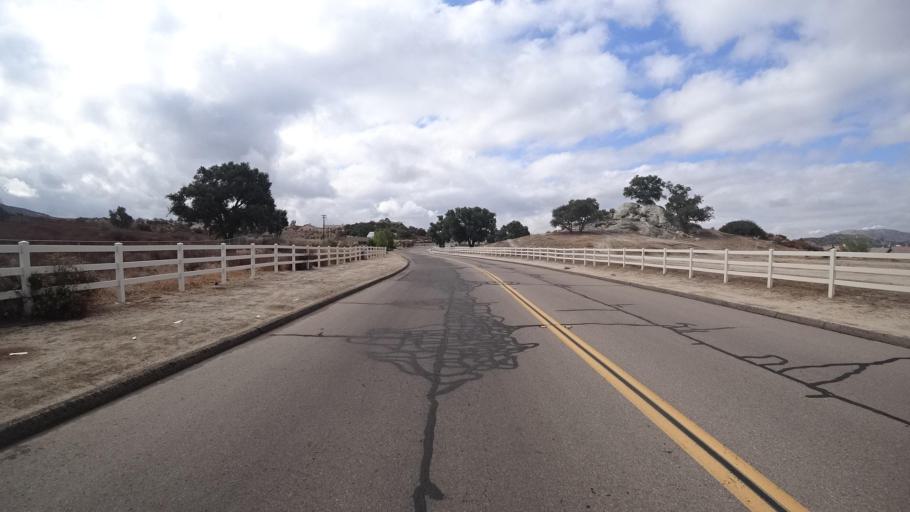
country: US
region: California
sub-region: San Diego County
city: Campo
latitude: 32.6227
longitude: -116.4632
